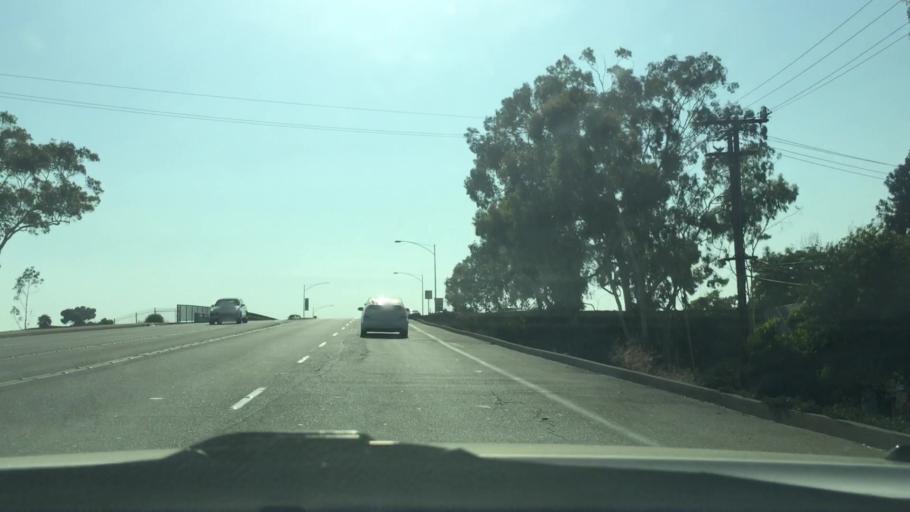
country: US
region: California
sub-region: Orange County
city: Midway City
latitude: 33.7447
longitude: -118.0030
